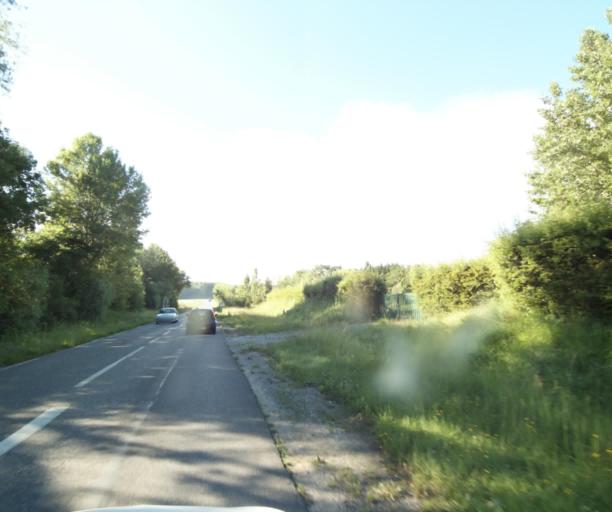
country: FR
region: Rhone-Alpes
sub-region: Departement de la Haute-Savoie
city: Douvaine
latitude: 46.3221
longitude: 6.2947
